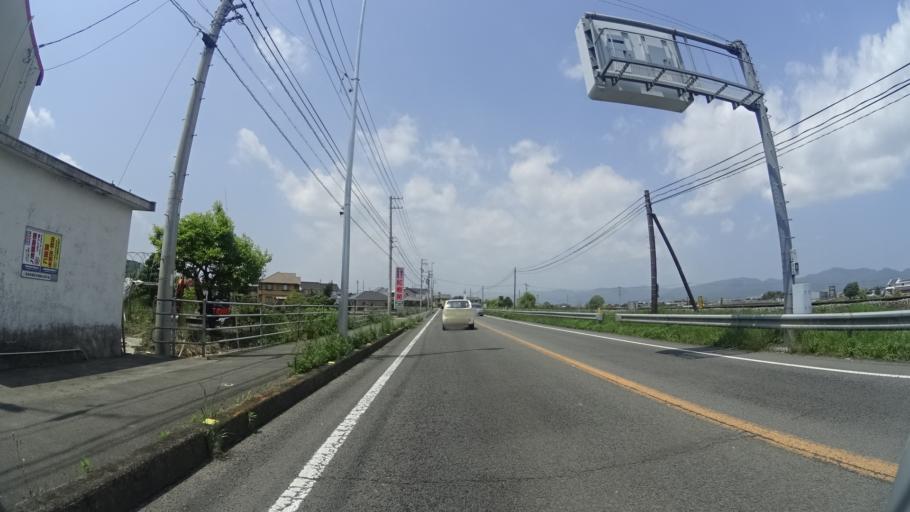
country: JP
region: Tokushima
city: Ishii
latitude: 34.0667
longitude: 134.4267
